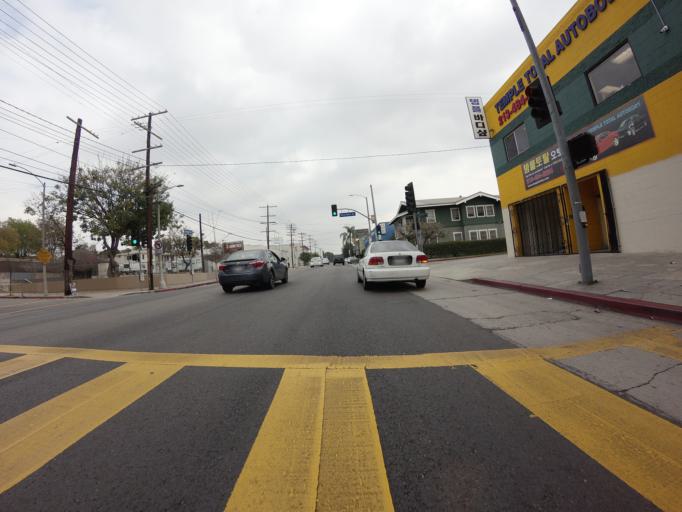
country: US
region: California
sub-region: Los Angeles County
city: Echo Park
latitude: 34.0709
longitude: -118.2703
